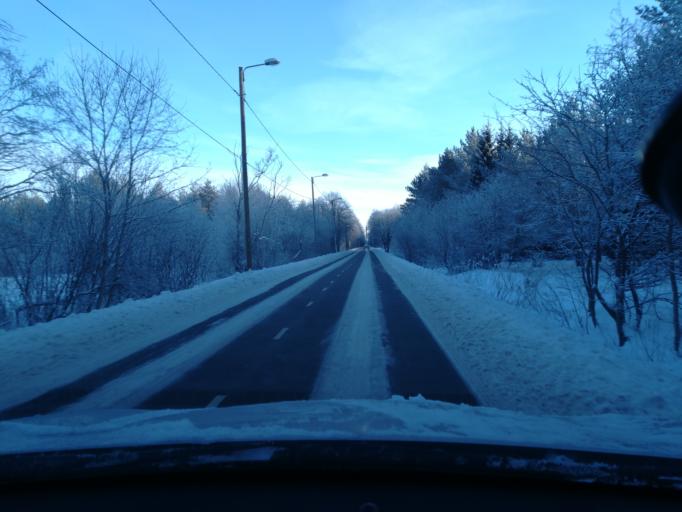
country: EE
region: Harju
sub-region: Saue vald
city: Laagri
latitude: 59.3911
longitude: 24.6111
